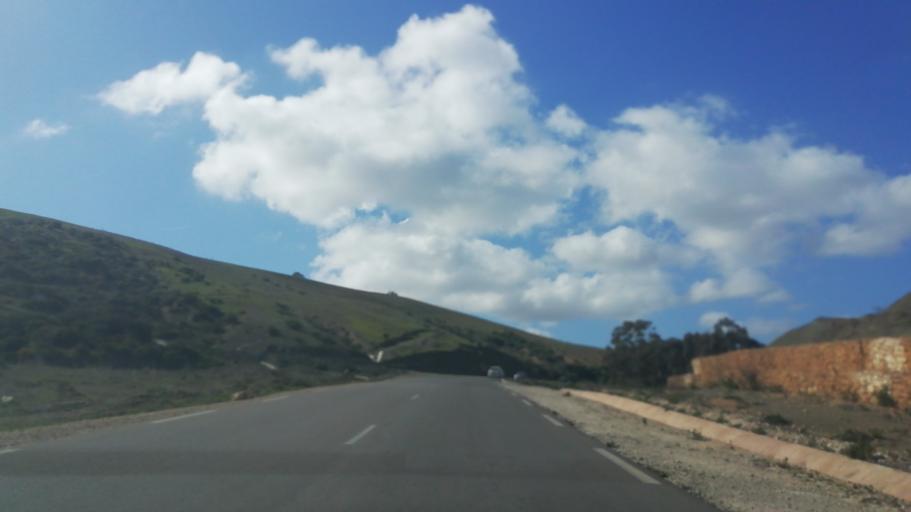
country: DZ
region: Relizane
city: Relizane
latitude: 36.0821
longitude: 0.4802
